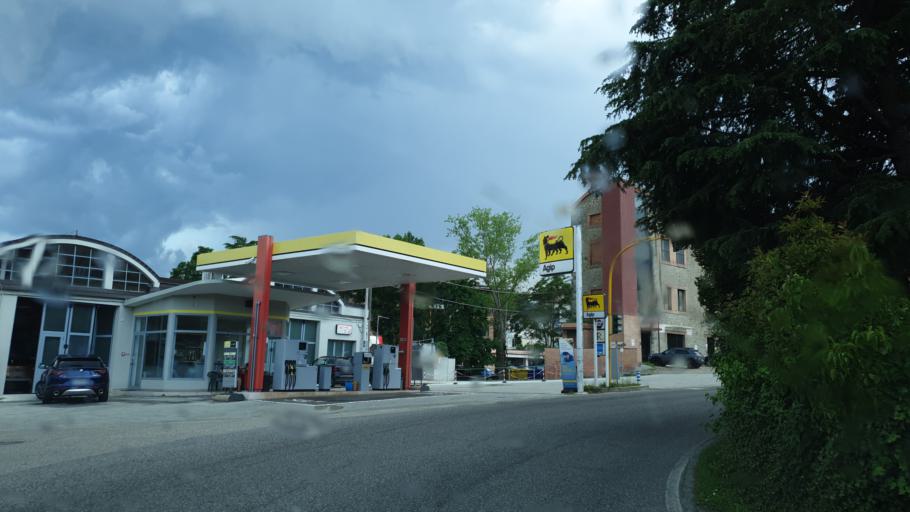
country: IT
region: Emilia-Romagna
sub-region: Provincia di Rimini
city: Novafeltria
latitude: 43.8977
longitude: 12.2890
